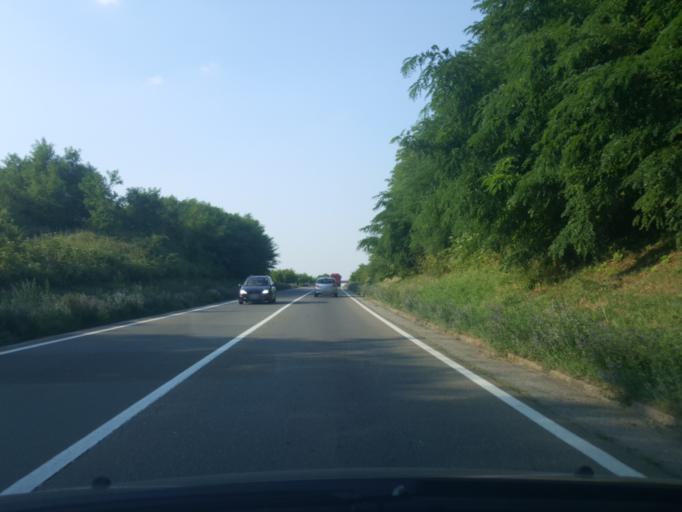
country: RS
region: Central Serbia
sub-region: Belgrade
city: Sopot
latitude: 44.5342
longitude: 20.6568
